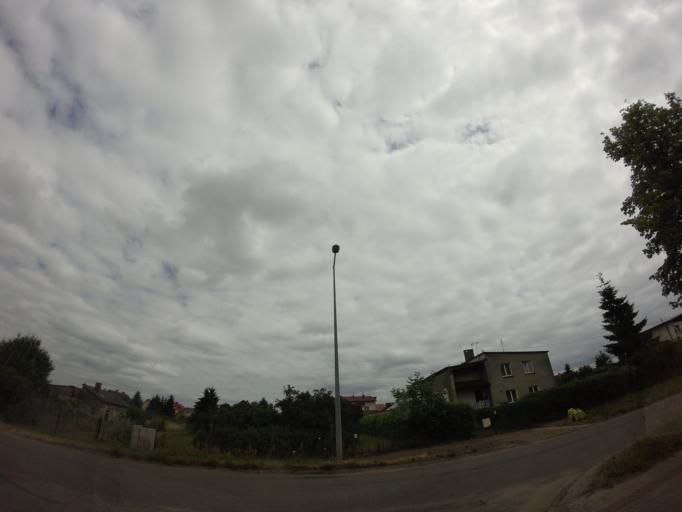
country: PL
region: Lubusz
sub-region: Powiat strzelecko-drezdenecki
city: Strzelce Krajenskie
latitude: 52.8792
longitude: 15.5447
